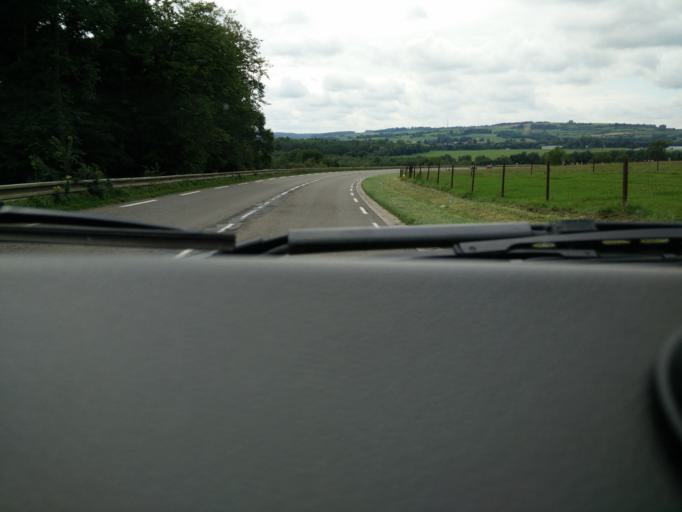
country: FR
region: Champagne-Ardenne
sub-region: Departement des Ardennes
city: Warcq
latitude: 49.7852
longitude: 4.6667
